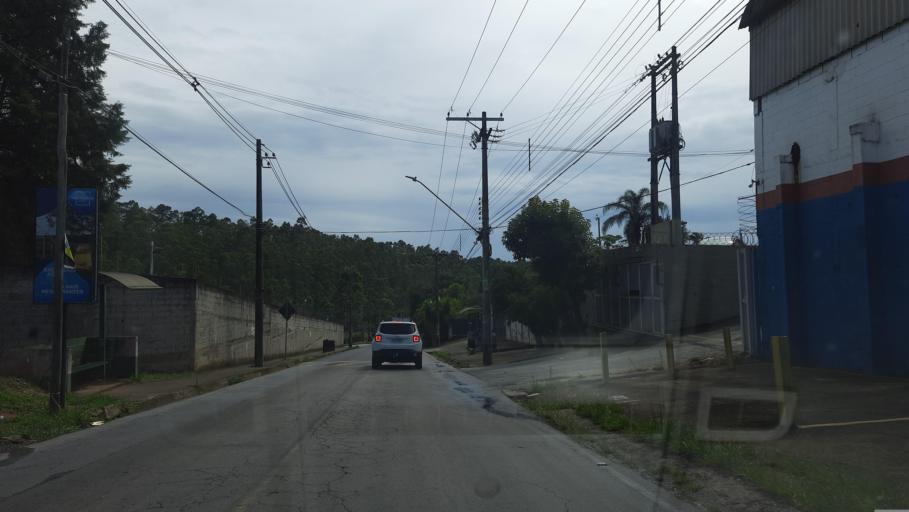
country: BR
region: Sao Paulo
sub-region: Caieiras
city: Caieiras
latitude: -23.3773
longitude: -46.7118
